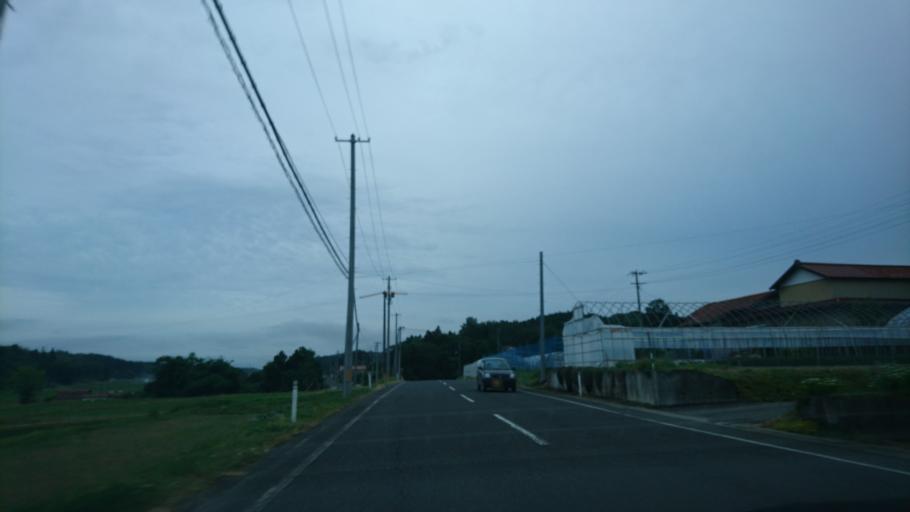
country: JP
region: Iwate
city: Ichinoseki
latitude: 38.9262
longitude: 141.1727
